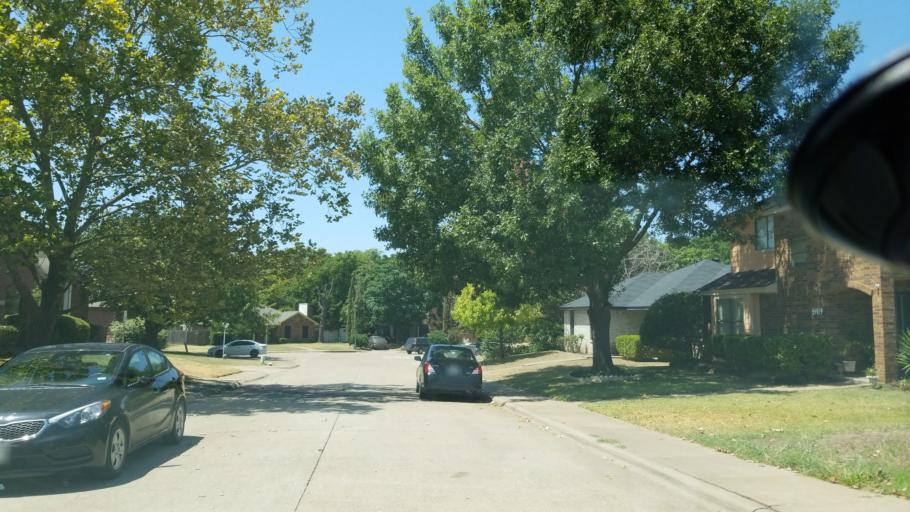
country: US
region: Texas
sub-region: Dallas County
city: Duncanville
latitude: 32.6374
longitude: -96.8886
